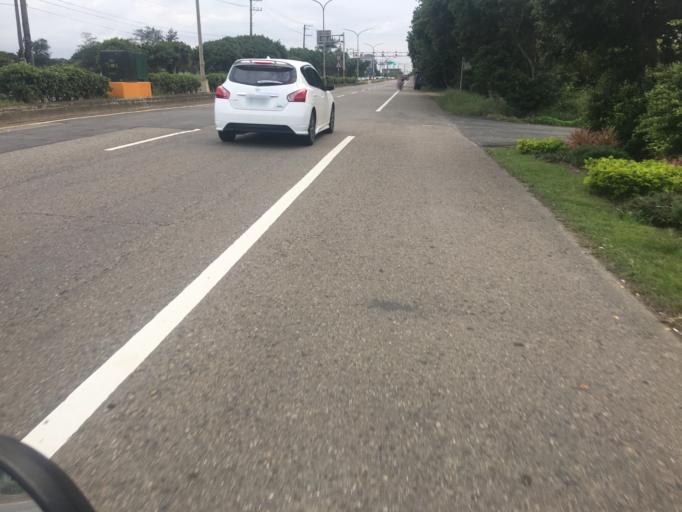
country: TW
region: Taiwan
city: Taoyuan City
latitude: 25.0923
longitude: 121.2314
